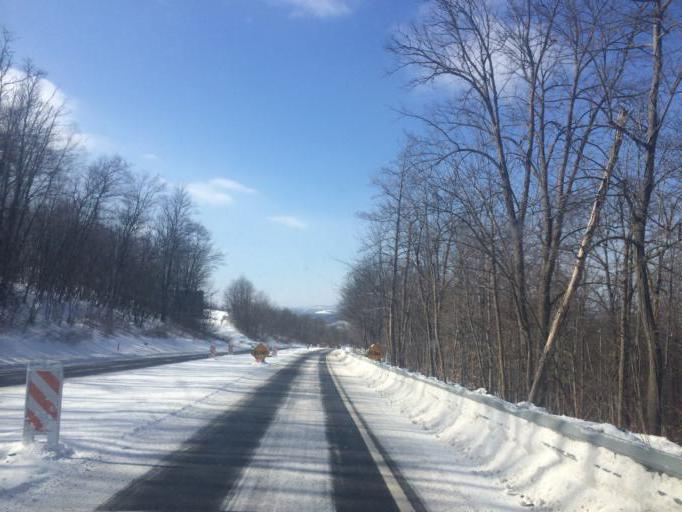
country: US
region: Pennsylvania
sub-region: Centre County
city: Stormstown
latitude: 40.8307
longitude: -77.9892
